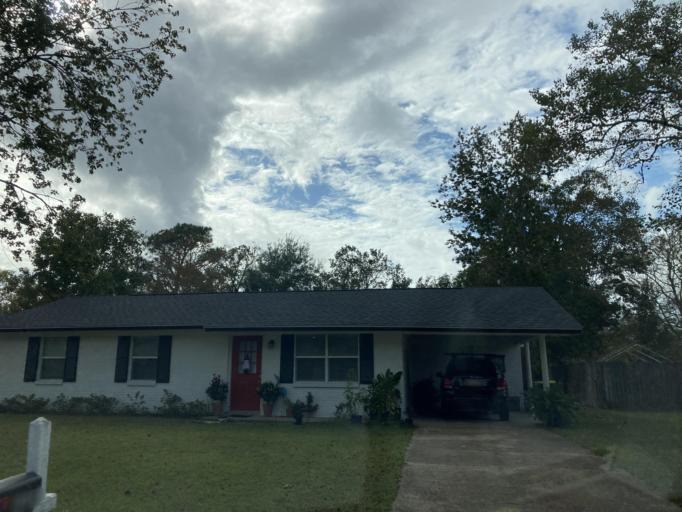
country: US
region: Mississippi
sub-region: Jackson County
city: Gulf Hills
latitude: 30.4364
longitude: -88.8255
